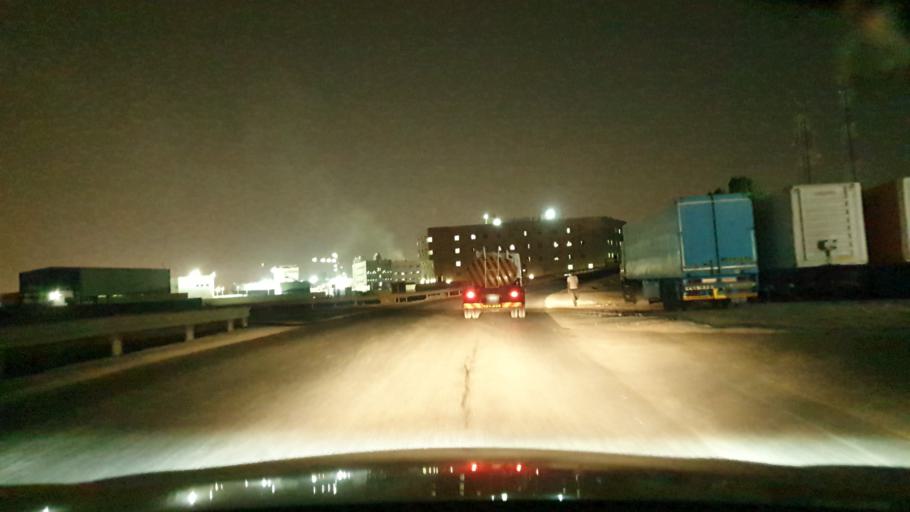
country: BH
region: Northern
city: Sitrah
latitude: 26.0935
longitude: 50.6149
